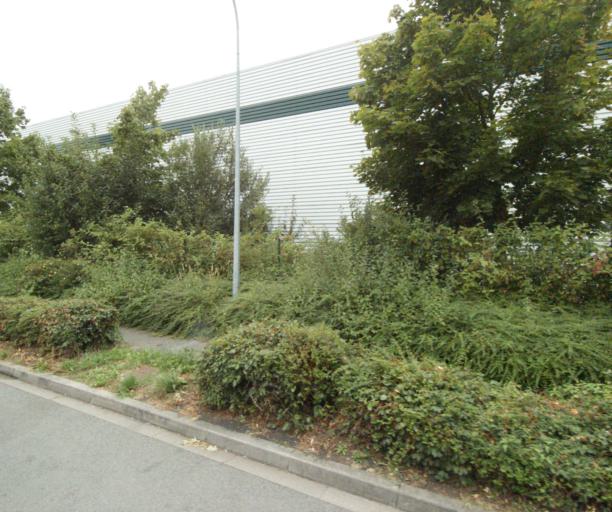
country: FR
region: Nord-Pas-de-Calais
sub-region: Departement du Nord
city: Sainghin-en-Melantois
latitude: 50.5798
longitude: 3.1448
